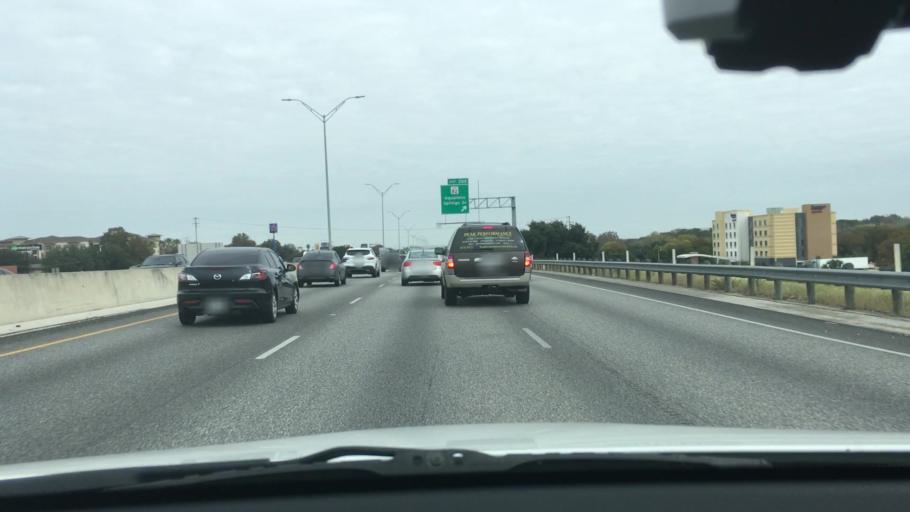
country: US
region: Texas
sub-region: Hays County
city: San Marcos
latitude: 29.8852
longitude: -97.9195
